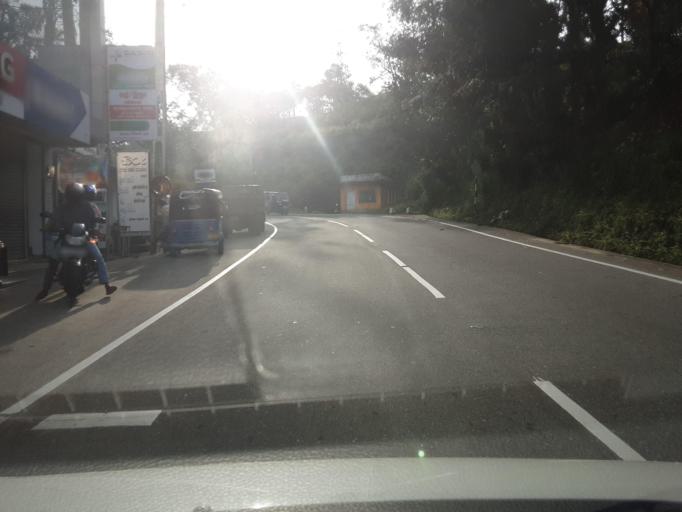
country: LK
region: Uva
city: Badulla
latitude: 6.9370
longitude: 80.9911
